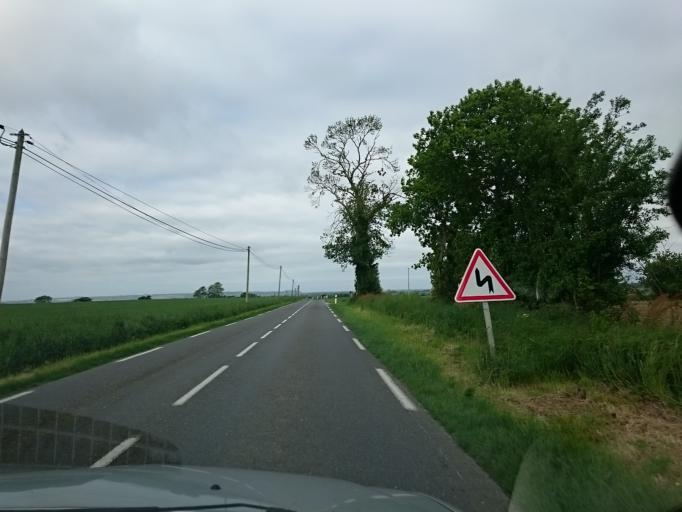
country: FR
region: Lower Normandy
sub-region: Departement de la Manche
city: Pontorson
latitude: 48.5558
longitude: -1.4467
